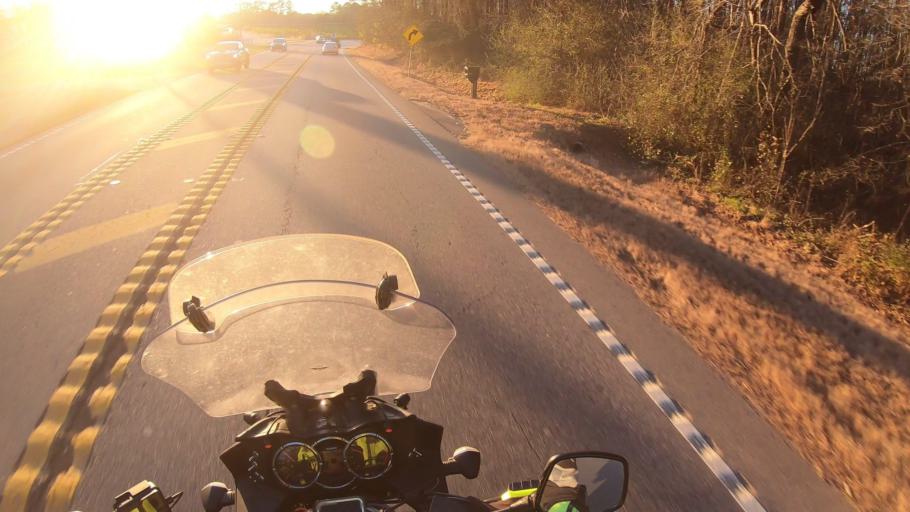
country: US
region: Georgia
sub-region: Forsyth County
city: Cumming
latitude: 34.2997
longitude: -84.1743
